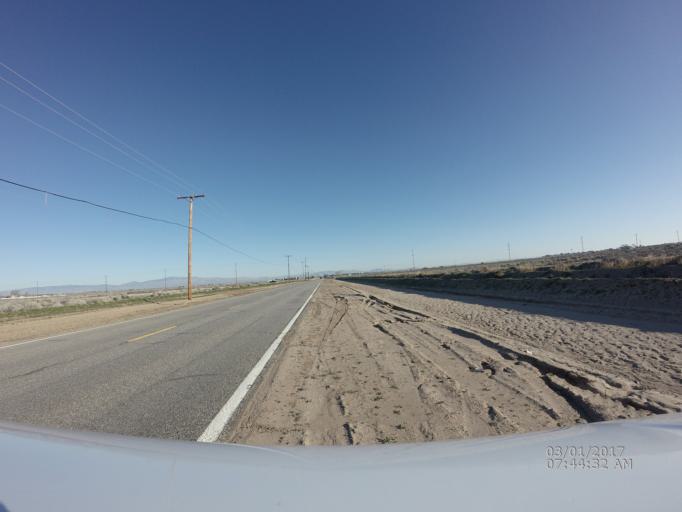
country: US
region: California
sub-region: Los Angeles County
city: Quartz Hill
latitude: 34.6874
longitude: -118.2541
